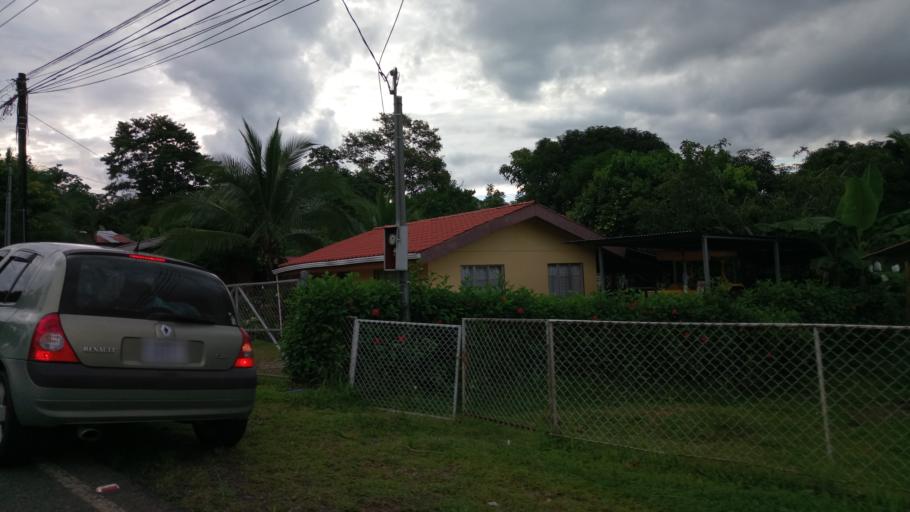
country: CR
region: Alajuela
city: Pocosol
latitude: 10.3660
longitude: -84.5862
